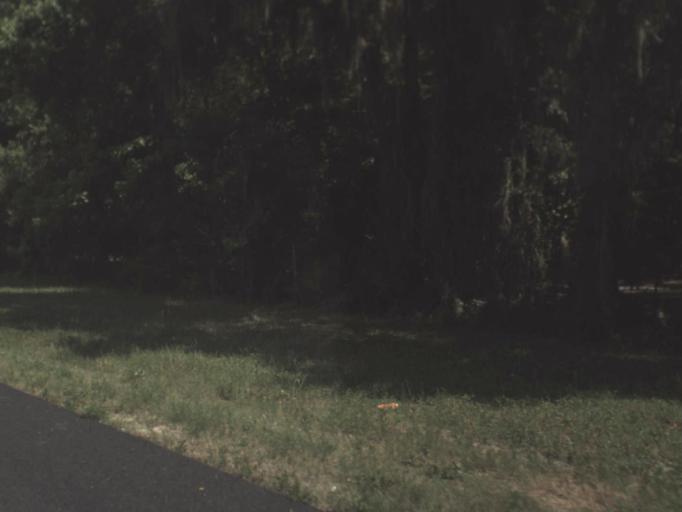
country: US
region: Florida
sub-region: Alachua County
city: Gainesville
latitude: 29.6106
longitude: -82.2453
